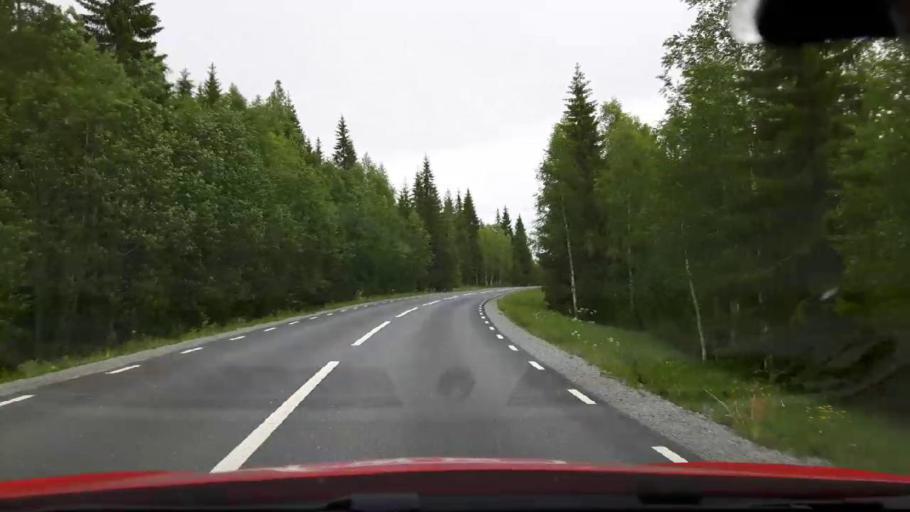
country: SE
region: Jaemtland
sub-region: OEstersunds Kommun
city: Lit
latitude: 63.7441
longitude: 14.8080
